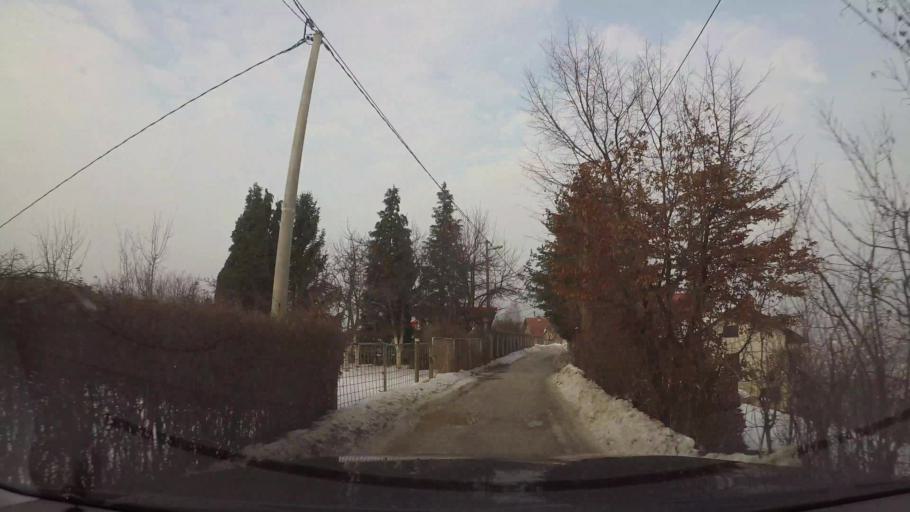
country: BA
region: Federation of Bosnia and Herzegovina
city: Hotonj
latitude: 43.8928
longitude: 18.3676
